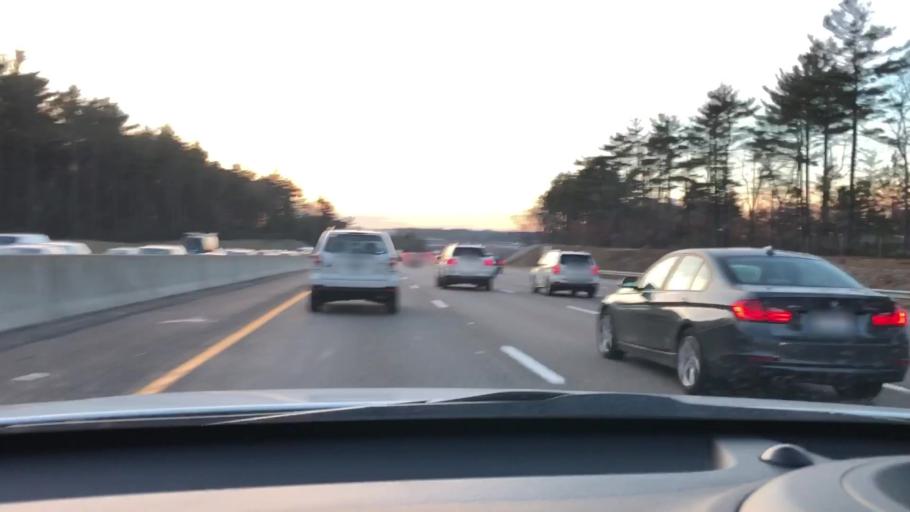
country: US
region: Massachusetts
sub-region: Norfolk County
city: Canton
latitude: 42.2028
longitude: -71.1251
